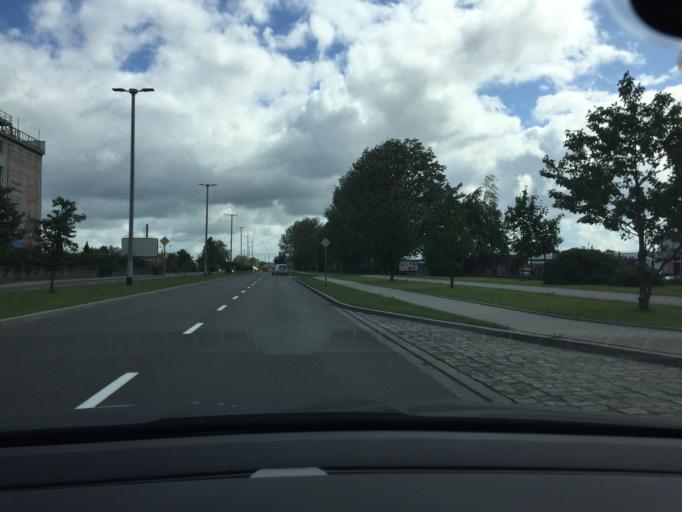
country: PL
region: West Pomeranian Voivodeship
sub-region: Koszalin
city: Koszalin
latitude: 54.1880
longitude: 16.1566
